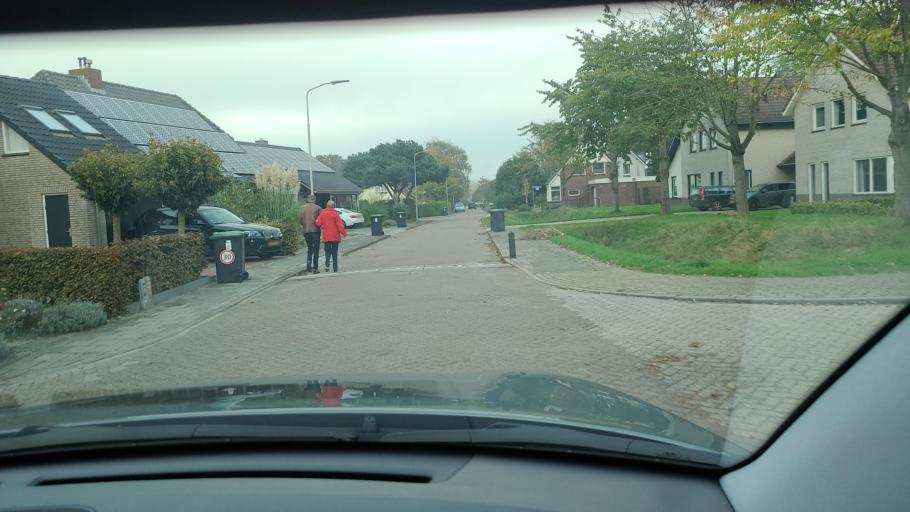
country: NL
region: North Brabant
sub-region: Gemeente Grave
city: Grave
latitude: 51.7574
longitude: 5.7841
